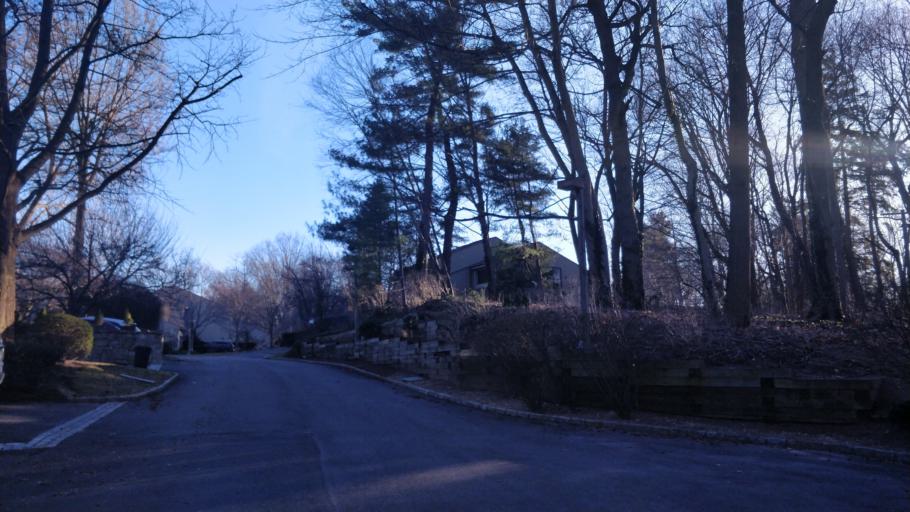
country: US
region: New York
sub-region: Nassau County
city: Glen Cove
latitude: 40.8687
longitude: -73.6520
